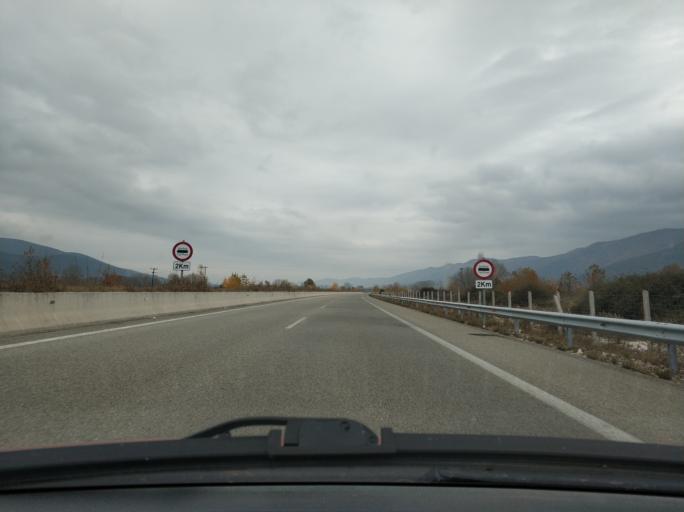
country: GR
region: East Macedonia and Thrace
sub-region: Nomos Kavalas
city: Nikisiani
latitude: 40.8492
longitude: 24.1350
